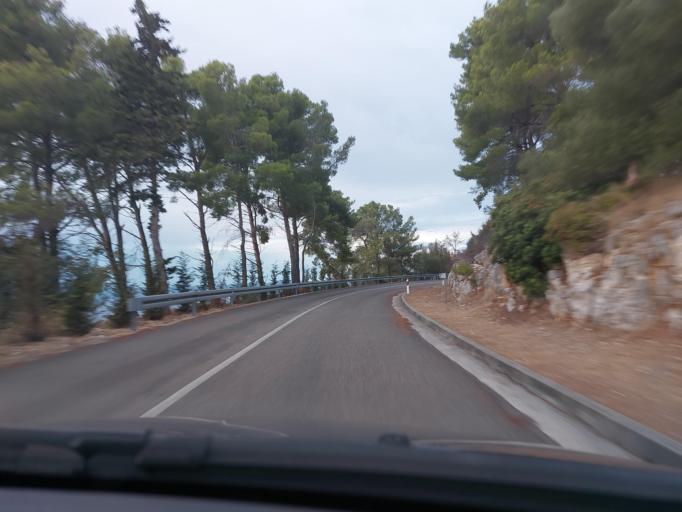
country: HR
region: Dubrovacko-Neretvanska
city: Smokvica
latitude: 42.7686
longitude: 16.8540
